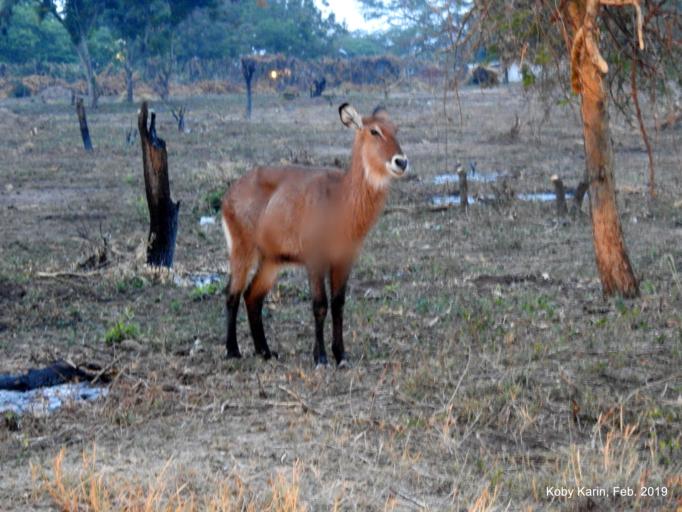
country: UG
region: Western Region
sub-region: Rubirizi District
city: Rubirizi
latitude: -0.1929
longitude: 29.9012
